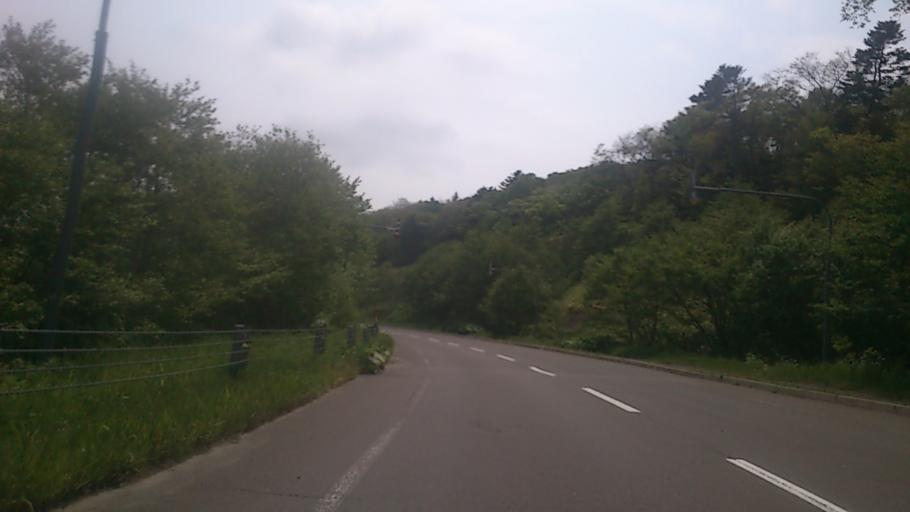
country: JP
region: Hokkaido
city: Nemuro
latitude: 43.2771
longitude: 145.5556
